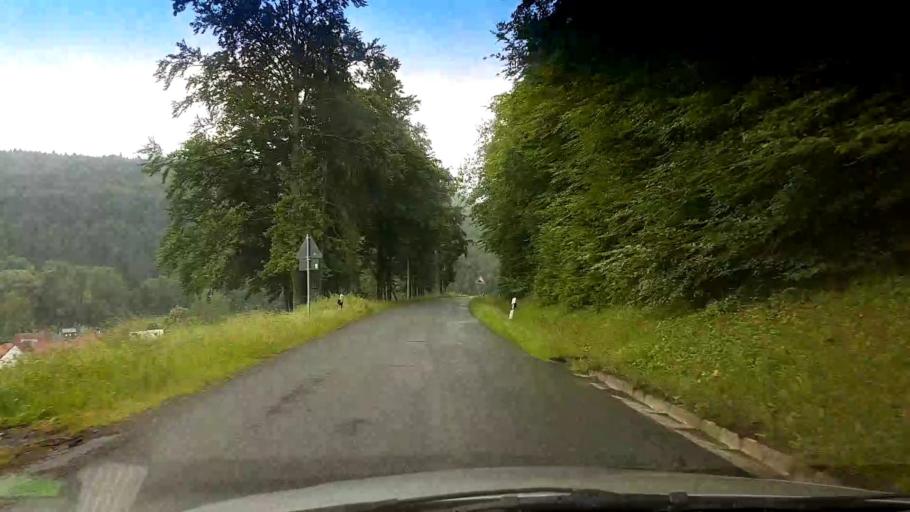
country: DE
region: Bavaria
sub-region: Upper Franconia
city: Altendorf
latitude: 50.0750
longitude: 11.1946
